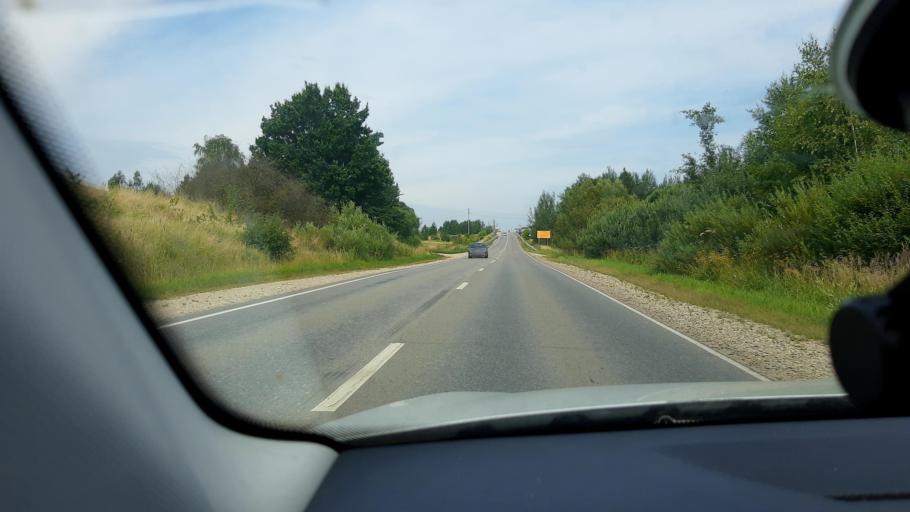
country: RU
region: Moskovskaya
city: Serpukhov
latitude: 54.8278
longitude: 37.4562
